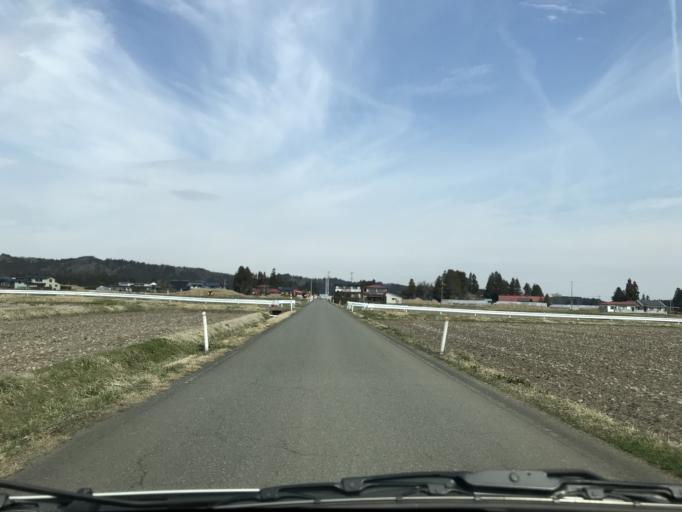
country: JP
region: Iwate
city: Mizusawa
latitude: 39.1328
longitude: 141.0480
